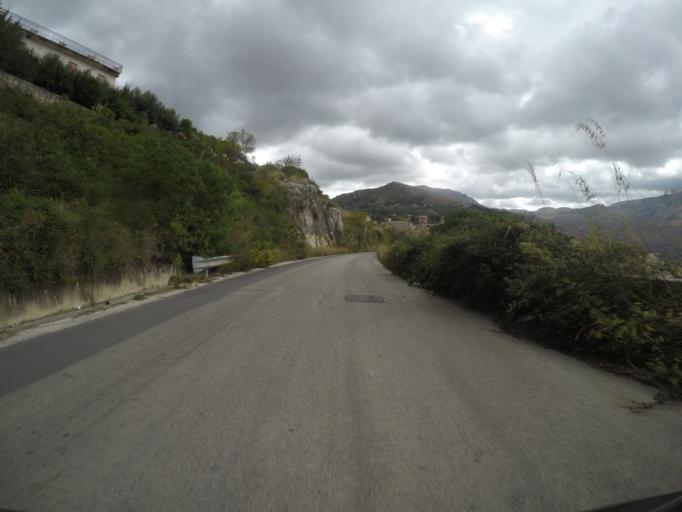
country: IT
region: Sicily
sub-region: Palermo
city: Montelepre
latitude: 38.0937
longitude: 13.1736
